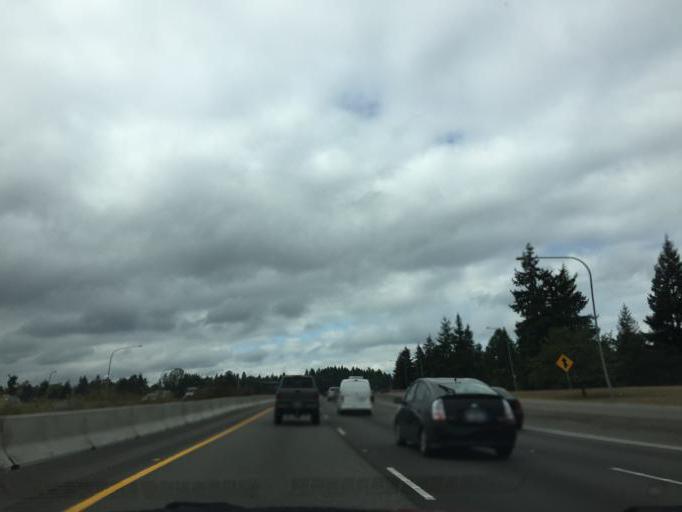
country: US
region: Washington
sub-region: Pierce County
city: Fort Lewis
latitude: 47.1053
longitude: -122.5853
